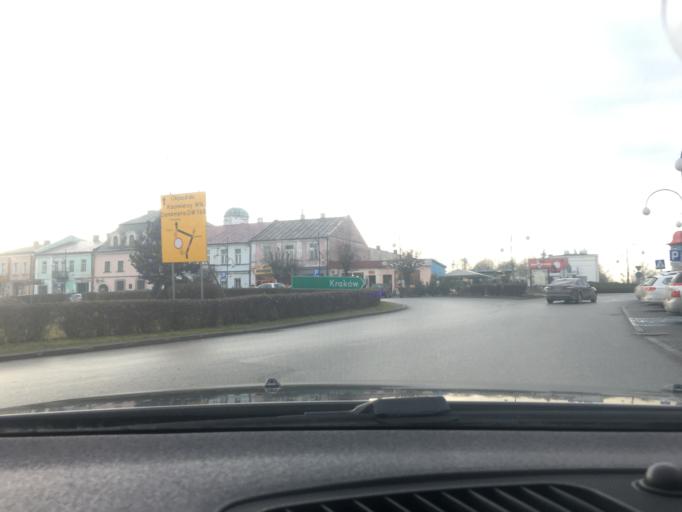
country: PL
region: Swietokrzyskie
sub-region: Powiat jedrzejowski
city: Jedrzejow
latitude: 50.6398
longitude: 20.3043
